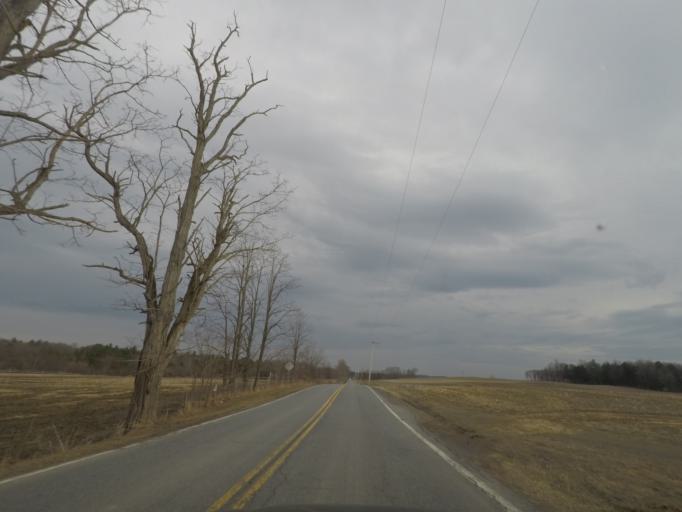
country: US
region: New York
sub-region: Washington County
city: Cambridge
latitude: 42.9630
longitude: -73.4605
